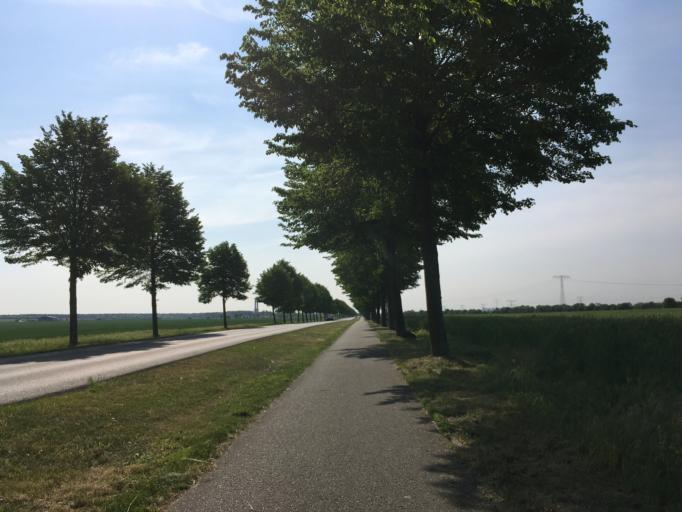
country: DE
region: Berlin
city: Wartenberg
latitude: 52.5986
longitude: 13.5371
